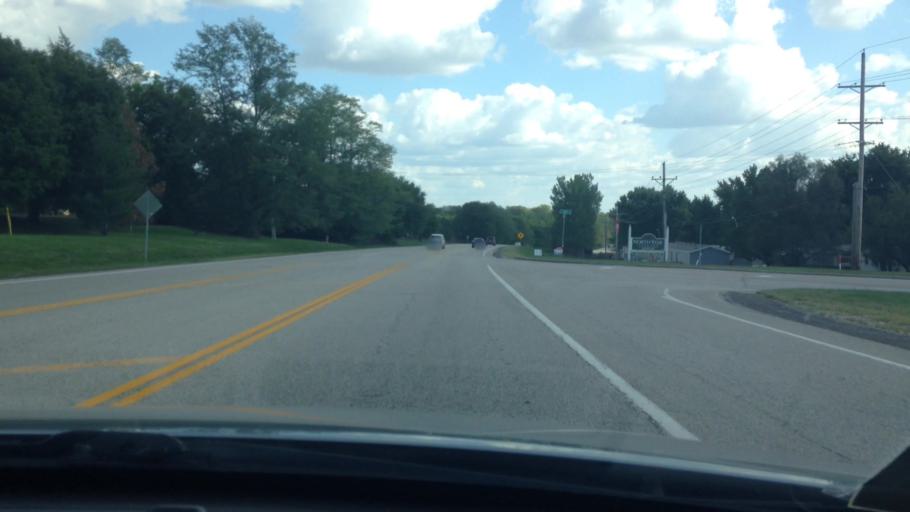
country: US
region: Missouri
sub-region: Clay County
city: Liberty
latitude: 39.2889
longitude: -94.4726
